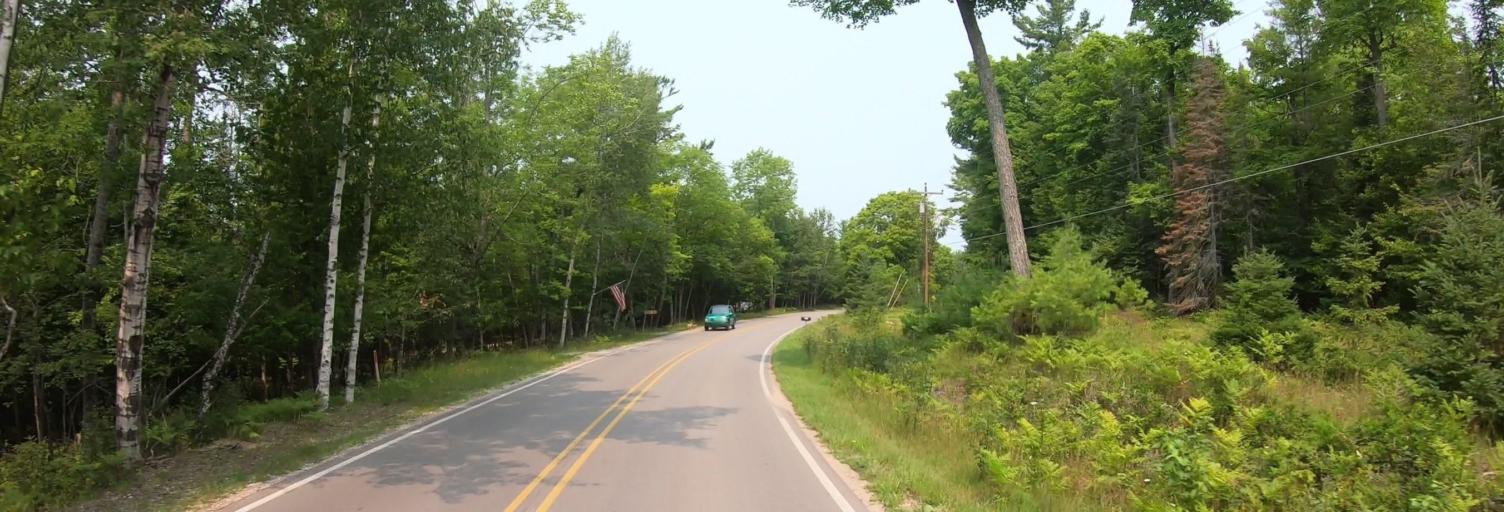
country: CA
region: Ontario
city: Thessalon
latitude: 46.0311
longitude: -83.7286
